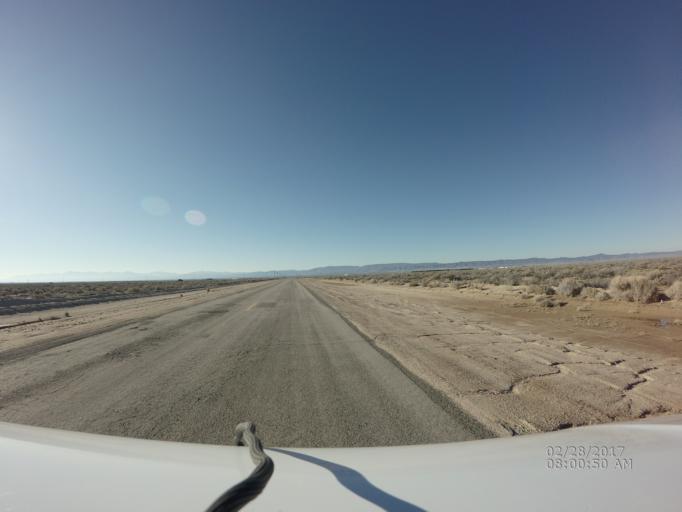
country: US
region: California
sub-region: Los Angeles County
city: Lancaster
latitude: 34.7659
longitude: -118.1845
